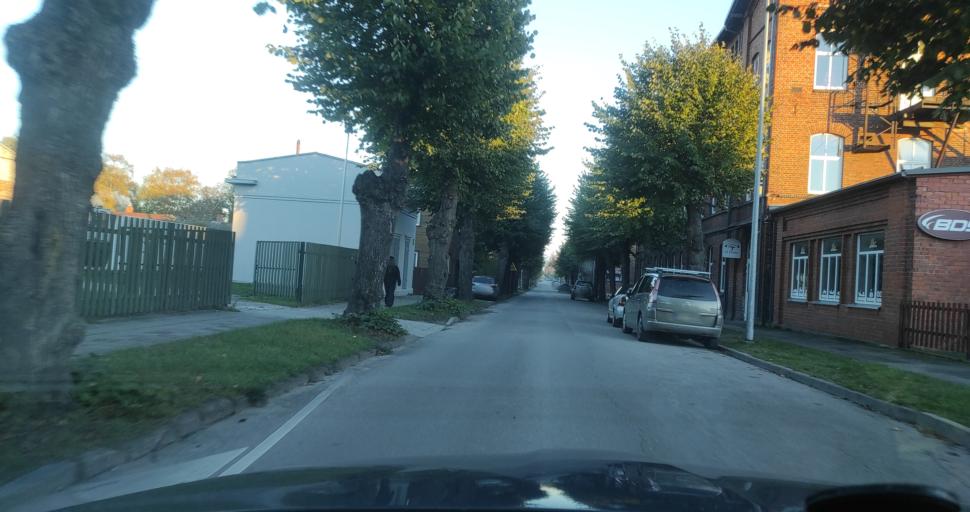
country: LV
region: Liepaja
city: Liepaja
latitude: 56.5009
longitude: 21.0124
